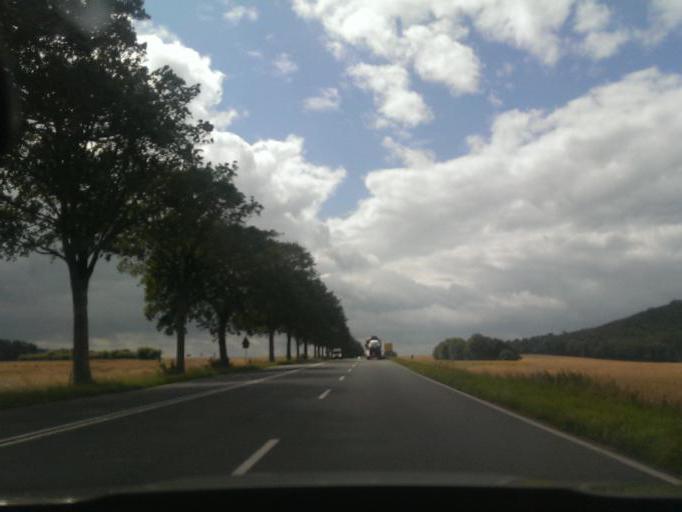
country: DE
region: Lower Saxony
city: Eschershausen
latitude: 51.9163
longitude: 9.6148
